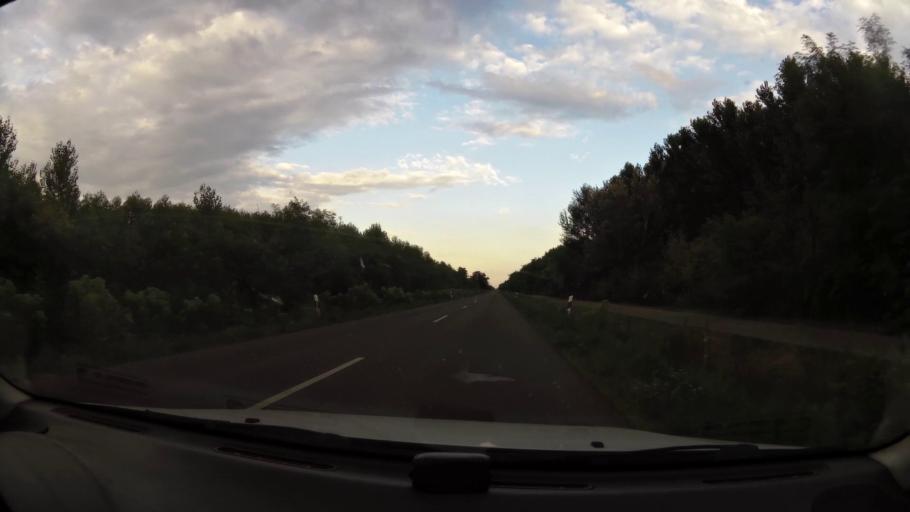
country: HU
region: Pest
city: Ujszilvas
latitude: 47.2857
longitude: 19.9126
